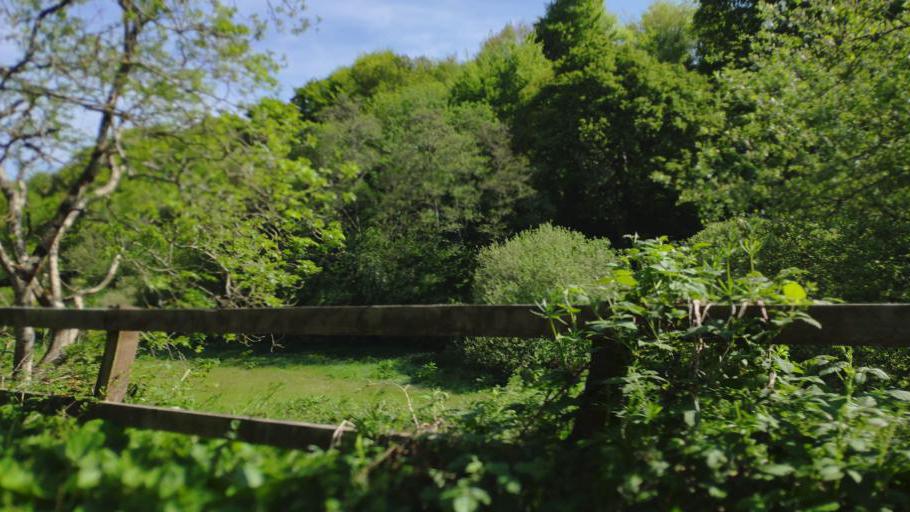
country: IE
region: Munster
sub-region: County Cork
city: Blarney
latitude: 51.9365
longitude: -8.5627
